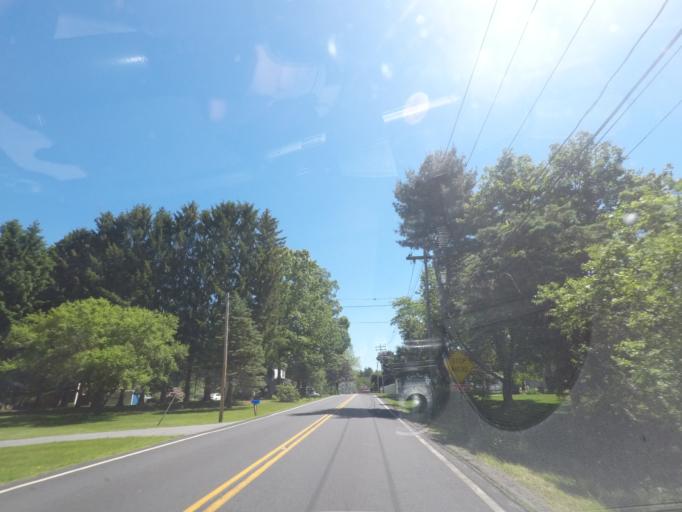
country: US
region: New York
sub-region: Saratoga County
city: Country Knolls
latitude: 42.9092
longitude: -73.8271
